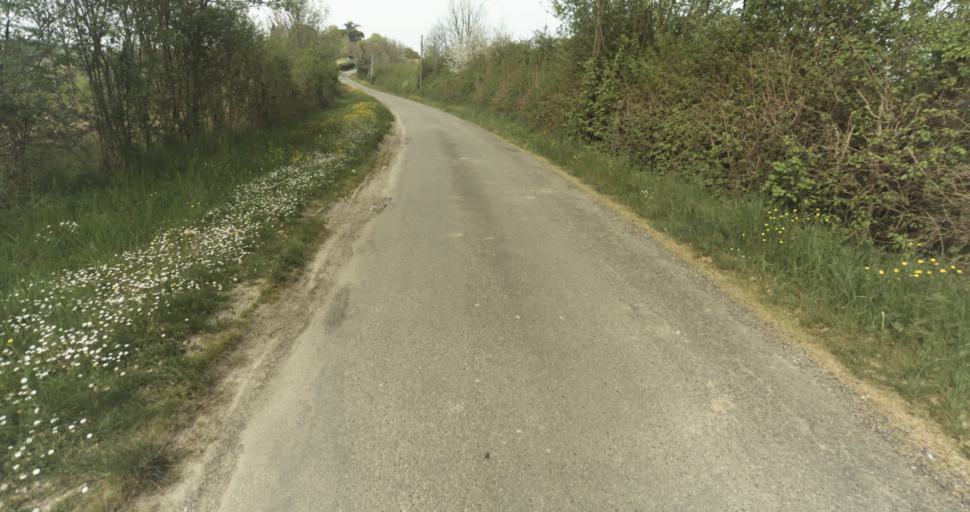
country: FR
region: Midi-Pyrenees
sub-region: Departement du Tarn-et-Garonne
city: Moissac
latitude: 44.1271
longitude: 1.1117
